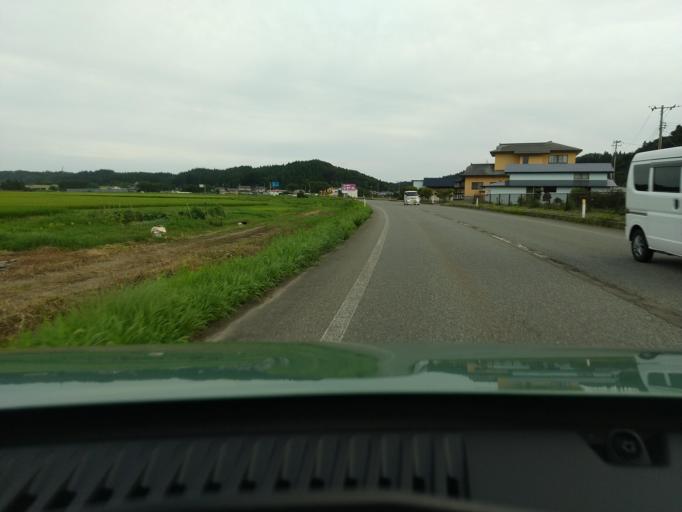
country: JP
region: Akita
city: Akita Shi
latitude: 39.7973
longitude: 140.0954
